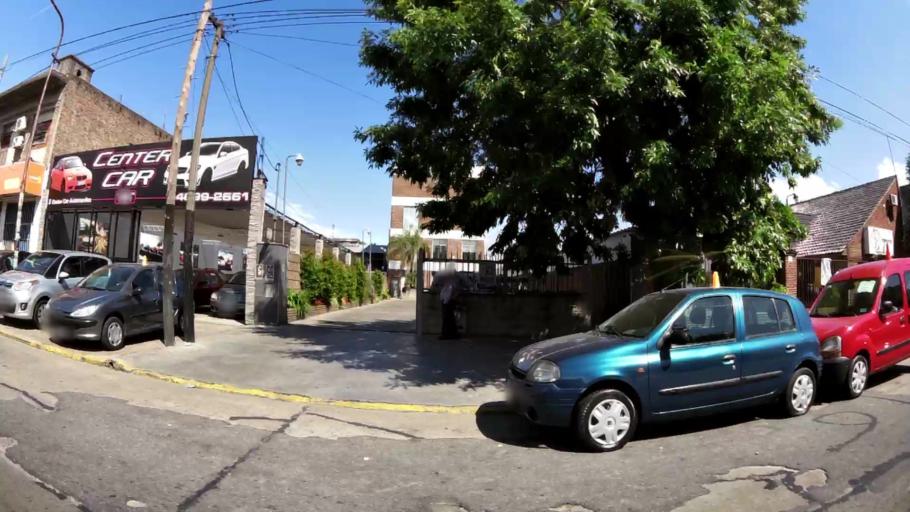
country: AR
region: Buenos Aires
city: San Justo
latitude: -34.6605
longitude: -58.5325
